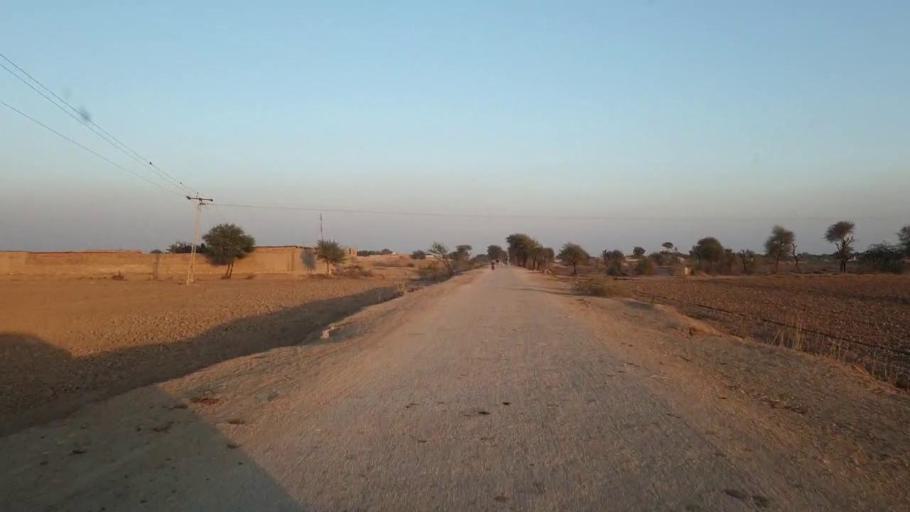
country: PK
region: Sindh
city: Chambar
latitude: 25.3048
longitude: 68.6592
